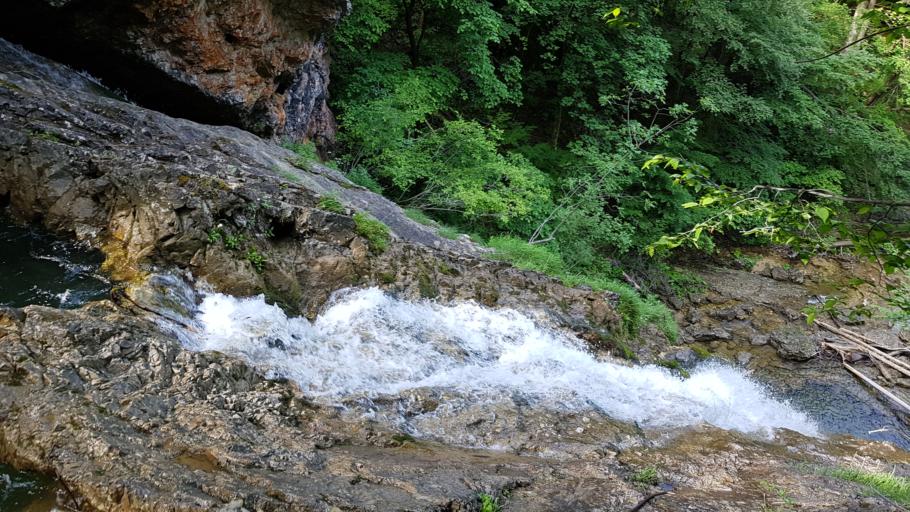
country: SI
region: Borovnica
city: Borovnica
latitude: 45.8819
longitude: 14.3696
